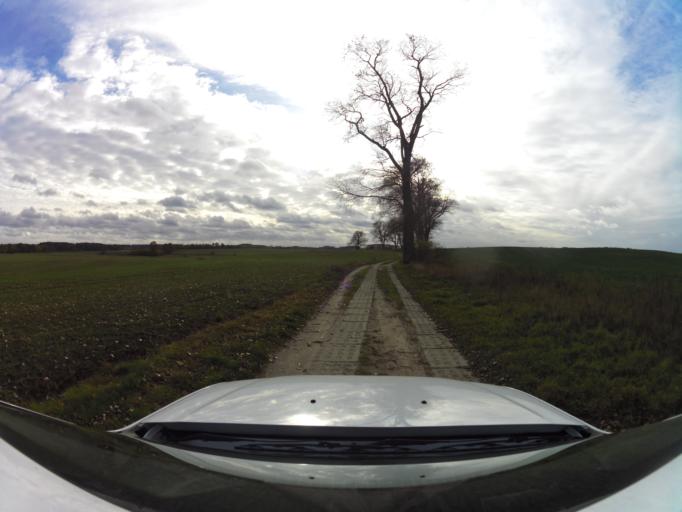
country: PL
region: West Pomeranian Voivodeship
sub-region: Powiat gryficki
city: Gryfice
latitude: 53.8860
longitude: 15.1179
